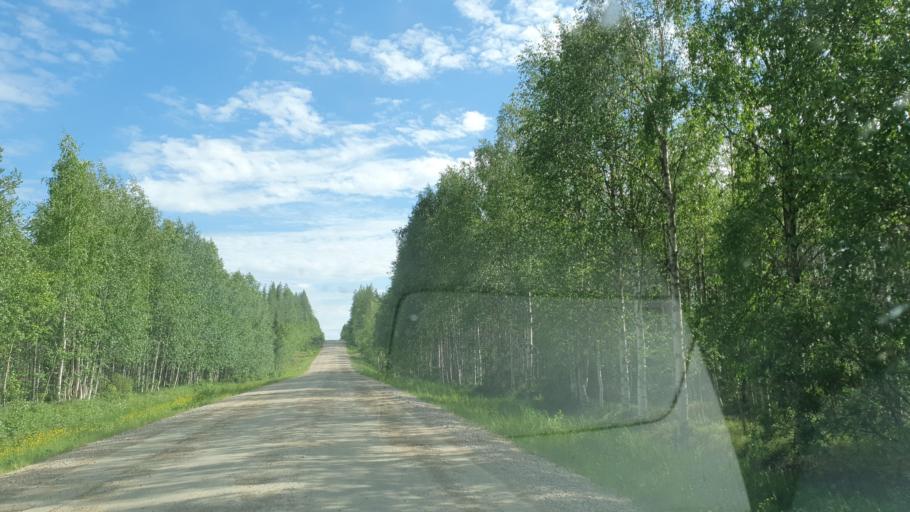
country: FI
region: Kainuu
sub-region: Kehys-Kainuu
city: Kuhmo
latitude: 64.4757
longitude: 29.5319
